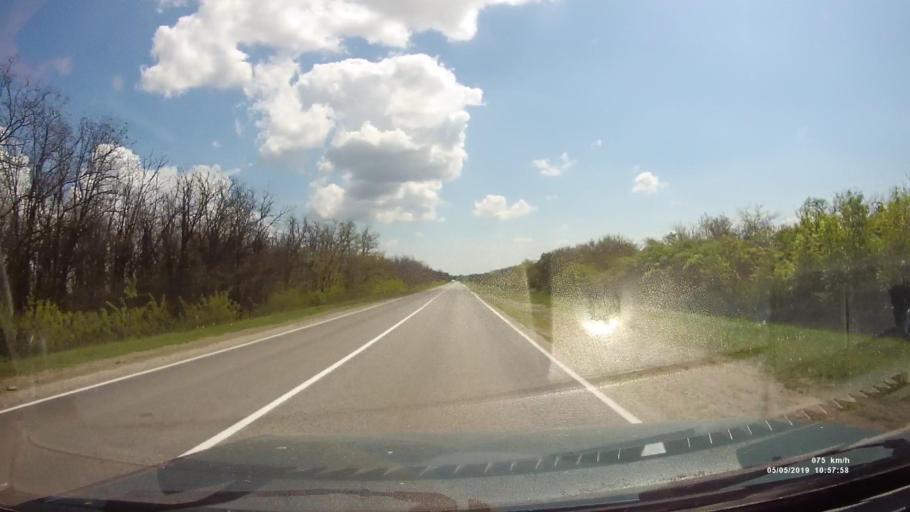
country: RU
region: Rostov
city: Ust'-Donetskiy
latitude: 47.6711
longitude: 40.8449
